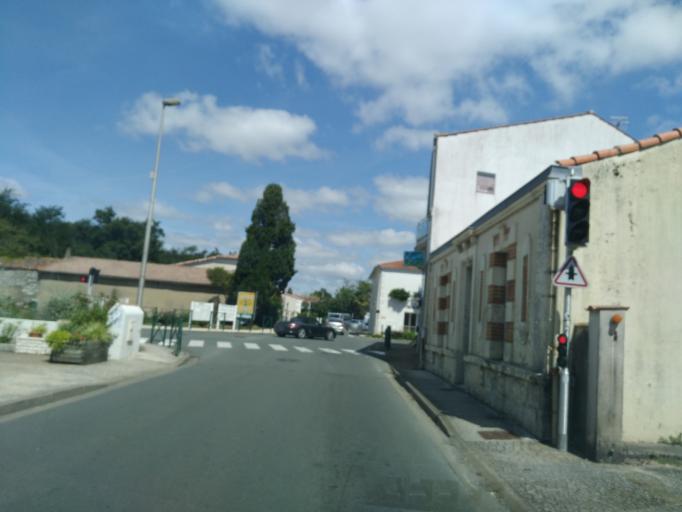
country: FR
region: Poitou-Charentes
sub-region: Departement de la Charente-Maritime
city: Breuillet
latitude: 45.6903
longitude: -1.0553
